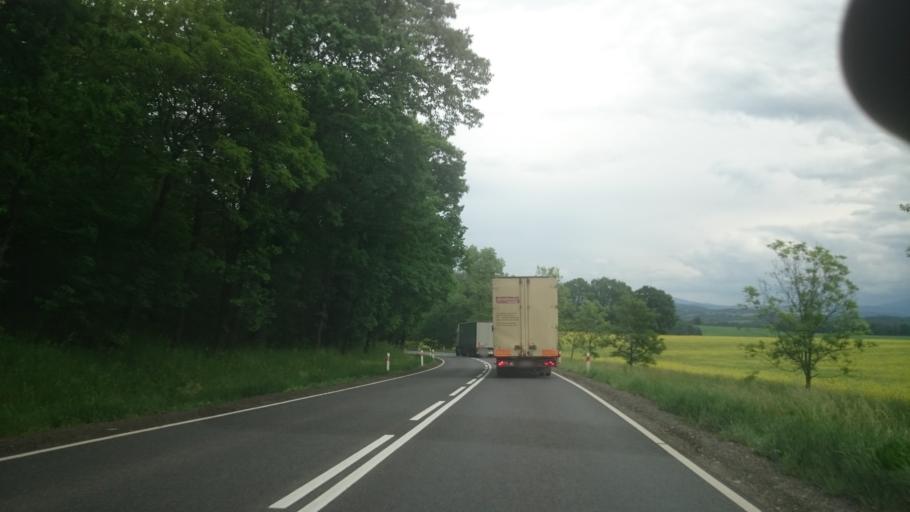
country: PL
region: Lower Silesian Voivodeship
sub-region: Powiat klodzki
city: Klodzko
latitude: 50.4313
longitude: 16.7149
